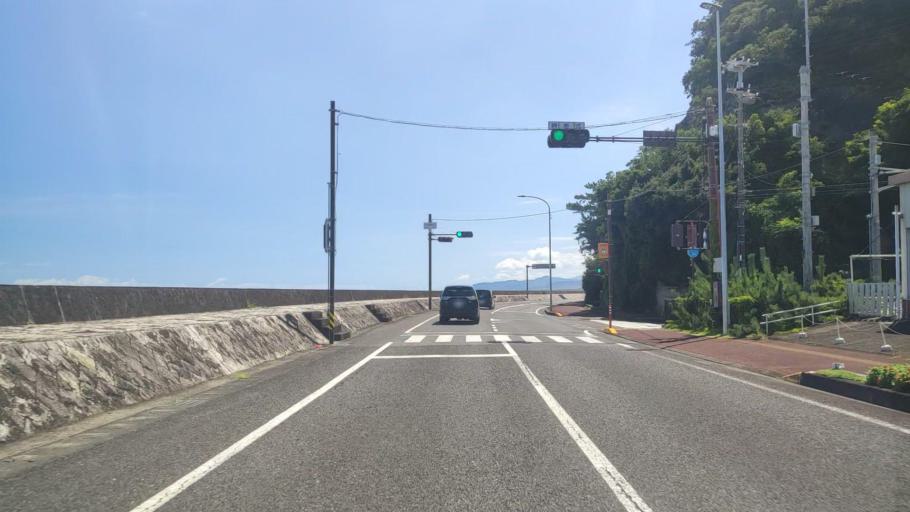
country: JP
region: Wakayama
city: Shingu
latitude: 33.8801
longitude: 136.0943
